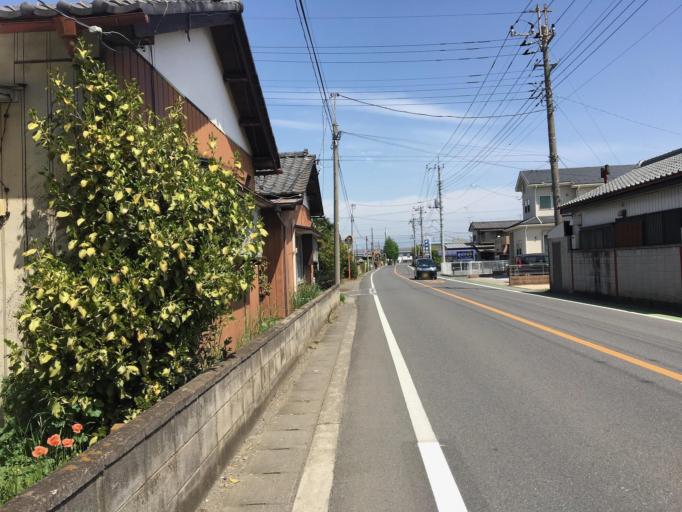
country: JP
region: Gunma
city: Sakai-nakajima
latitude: 36.2743
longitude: 139.2658
